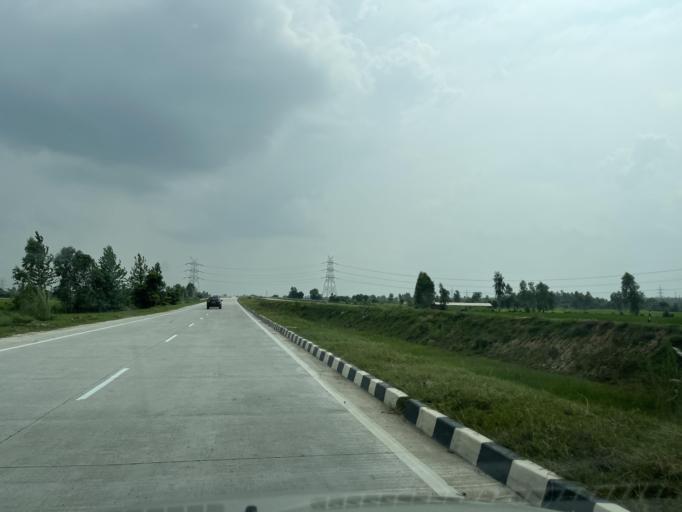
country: IN
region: Uttarakhand
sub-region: Udham Singh Nagar
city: Jaspur
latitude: 29.2762
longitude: 78.8681
